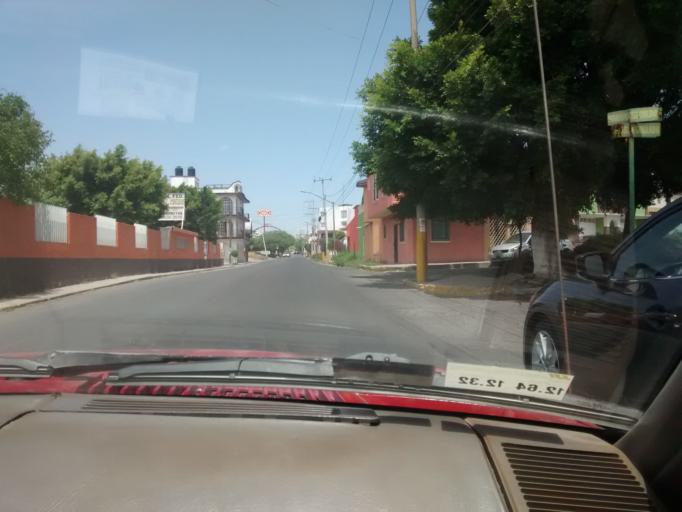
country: MX
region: Puebla
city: Tehuacan
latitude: 18.4604
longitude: -97.4122
